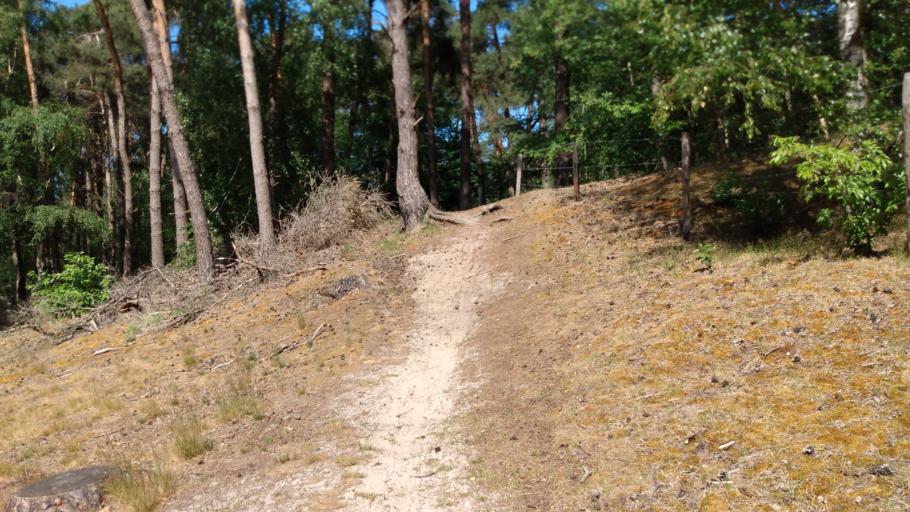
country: NL
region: North Brabant
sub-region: Gemeente Oisterwijk
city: Oisterwijk
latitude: 51.5573
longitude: 5.1629
